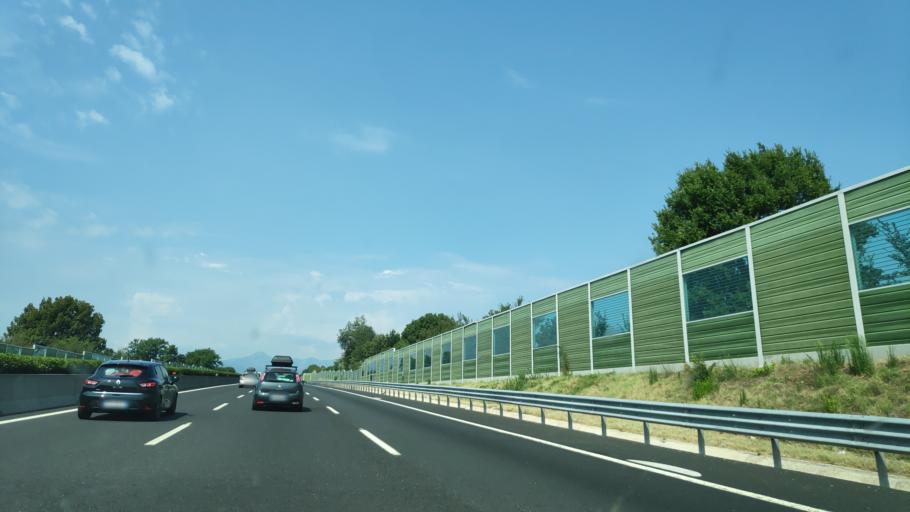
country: IT
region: Latium
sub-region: Provincia di Frosinone
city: Pofi
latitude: 41.5535
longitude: 13.4394
